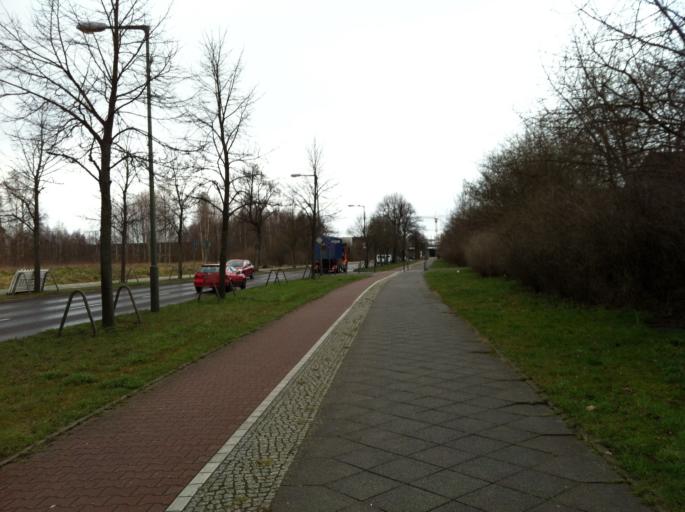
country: DE
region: Berlin
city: Karow
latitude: 52.6201
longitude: 13.4894
